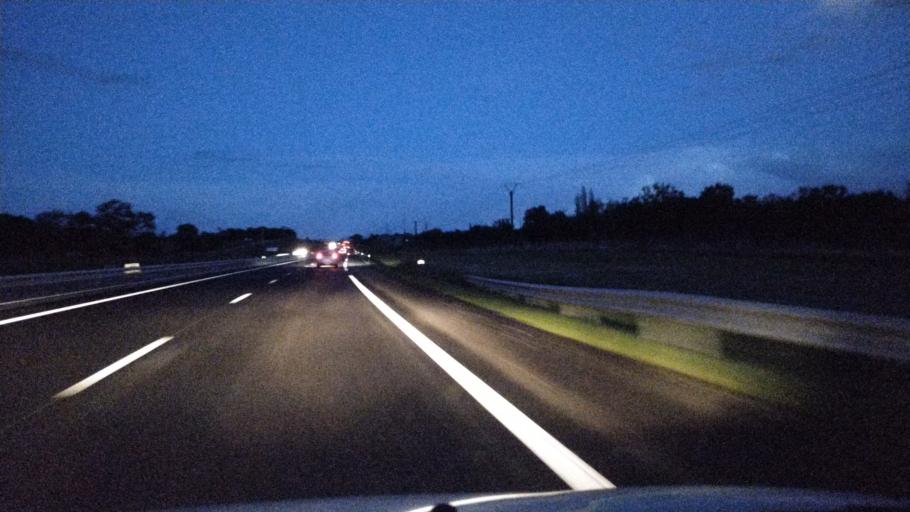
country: FR
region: Brittany
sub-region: Departement d'Ille-et-Vilaine
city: Quedillac
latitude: 48.1904
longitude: -2.1337
